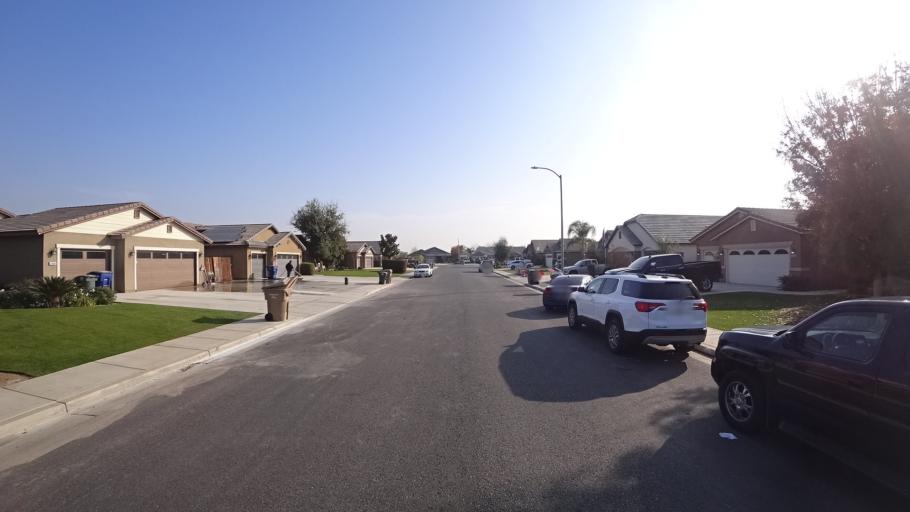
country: US
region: California
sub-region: Kern County
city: Greenacres
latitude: 35.4344
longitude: -119.1209
